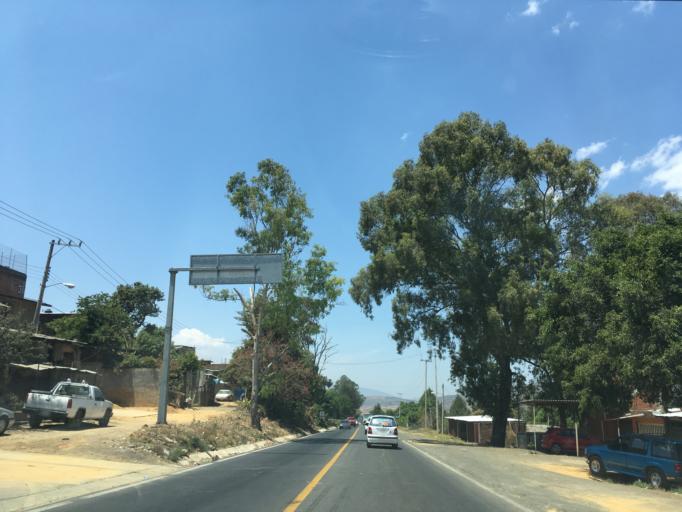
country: MX
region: Michoacan
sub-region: Chilchota
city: Tacuro (Santa Maria Tacuro)
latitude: 19.8522
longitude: -102.0338
